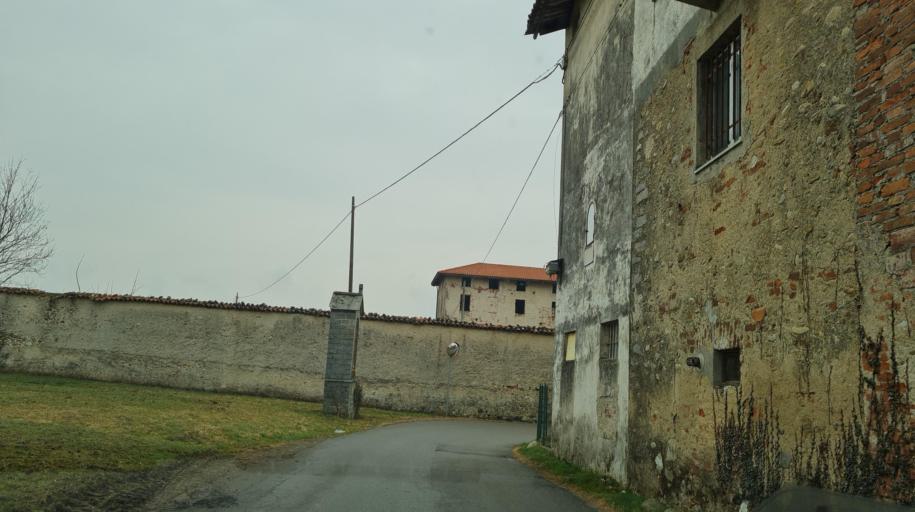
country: IT
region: Piedmont
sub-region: Provincia di Biella
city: Borriana
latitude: 45.5119
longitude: 8.0274
